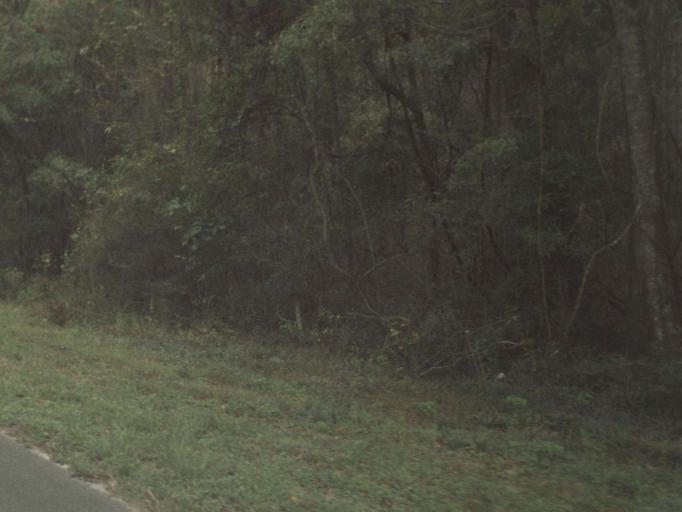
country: US
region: Florida
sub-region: Leon County
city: Woodville
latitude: 30.2797
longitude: -84.2401
